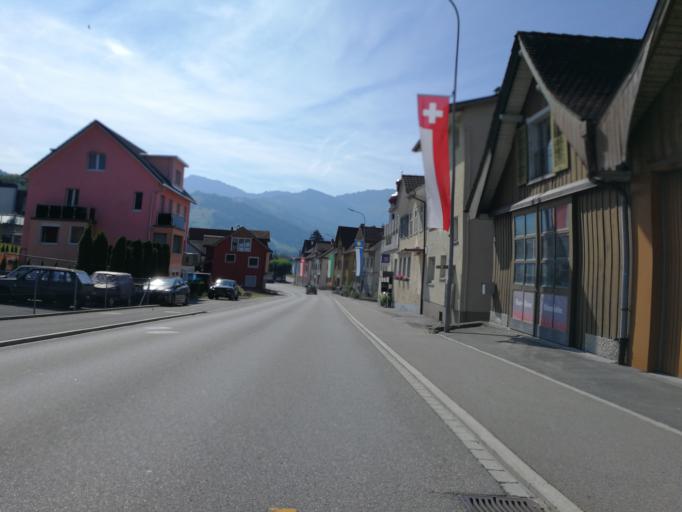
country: CH
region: Saint Gallen
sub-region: Wahlkreis See-Gaster
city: Gommiswald
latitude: 47.2325
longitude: 9.0213
